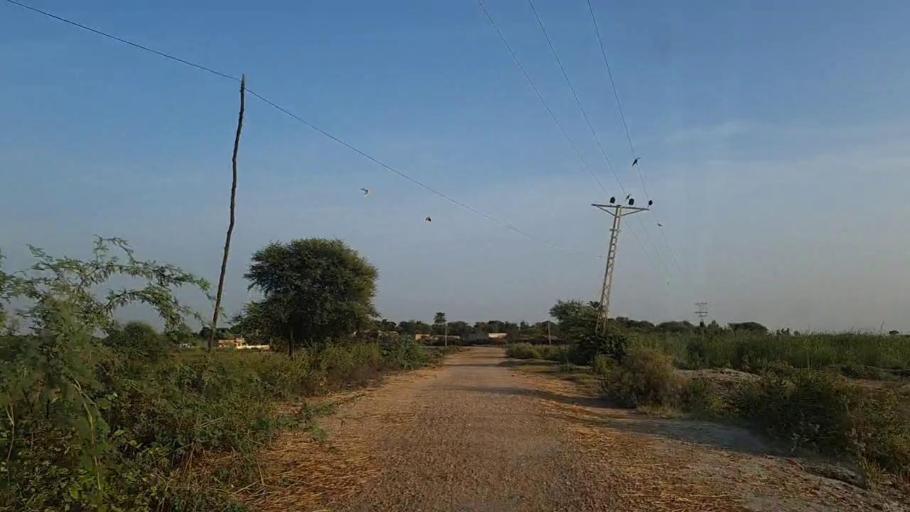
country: PK
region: Sindh
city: Daro Mehar
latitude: 24.6145
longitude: 68.0937
